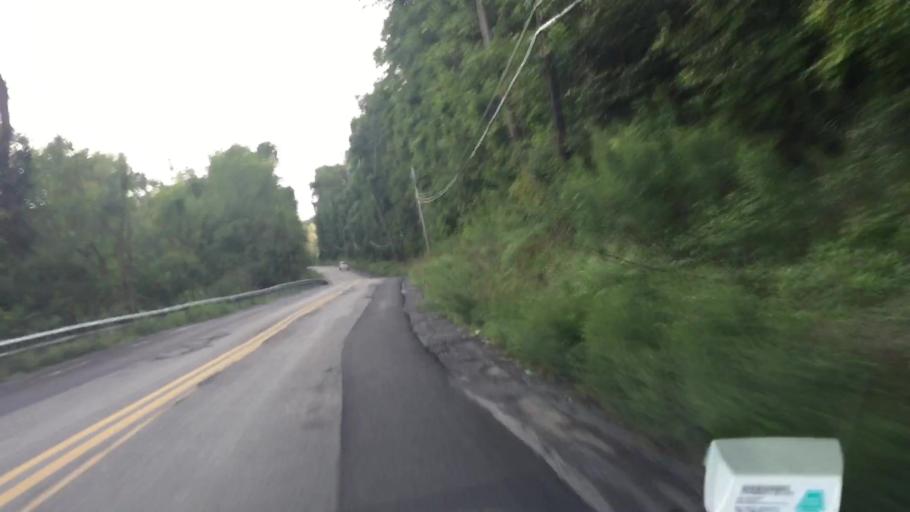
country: US
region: Pennsylvania
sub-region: Allegheny County
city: Franklin Park
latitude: 40.5560
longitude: -80.0580
